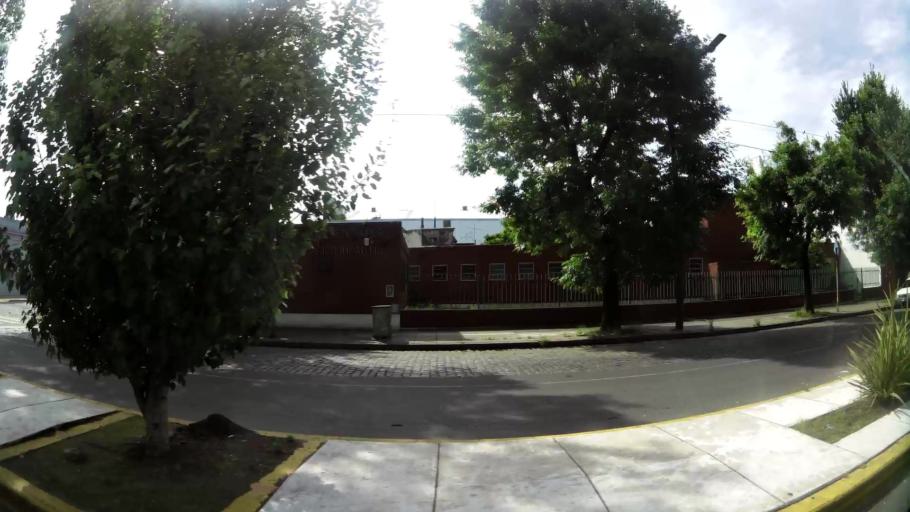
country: AR
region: Buenos Aires F.D.
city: Villa Lugano
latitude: -34.6656
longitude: -58.5040
